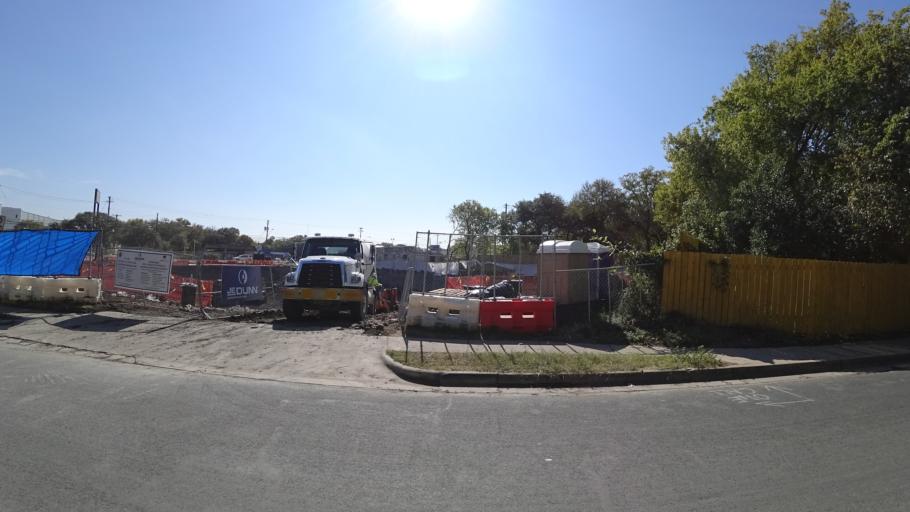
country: US
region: Texas
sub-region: Travis County
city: Austin
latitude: 30.2499
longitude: -97.7682
